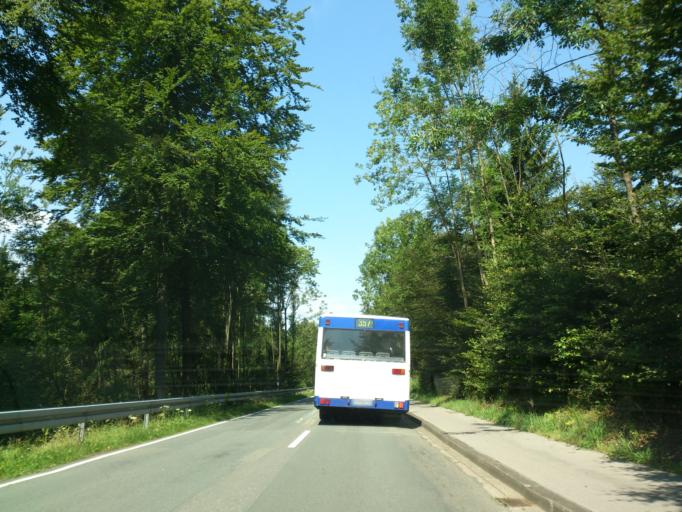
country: DE
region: North Rhine-Westphalia
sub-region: Regierungsbezirk Detmold
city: Horn
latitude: 51.8438
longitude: 8.9320
